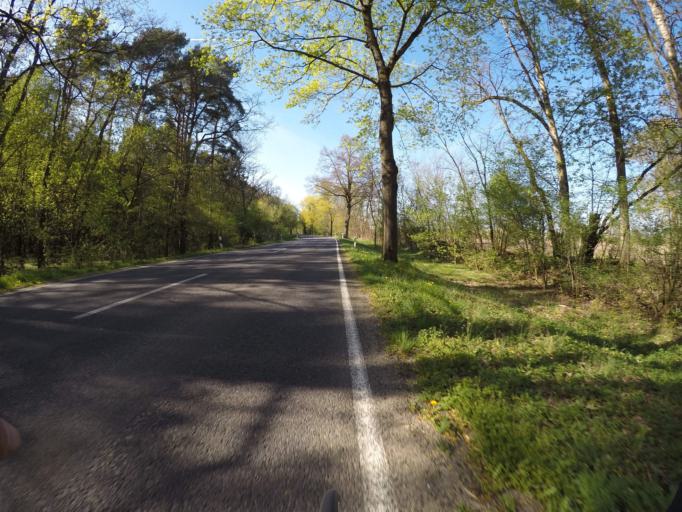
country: DE
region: Brandenburg
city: Grunheide
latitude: 52.4630
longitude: 13.8607
